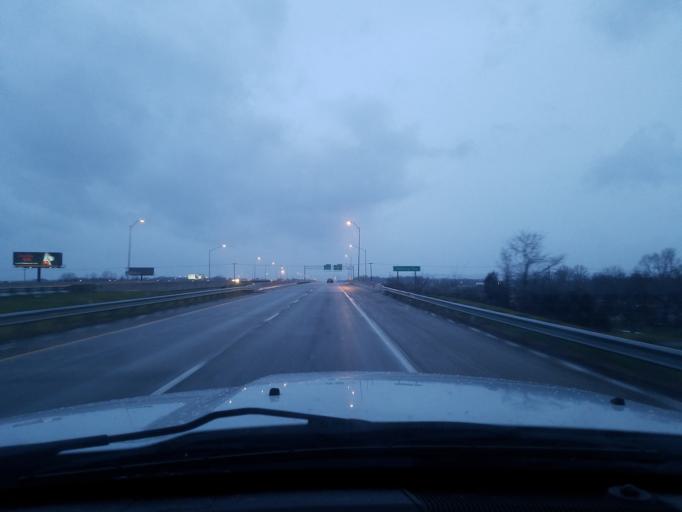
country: US
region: Indiana
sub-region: Clark County
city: Clarksville
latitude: 38.3462
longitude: -85.7443
